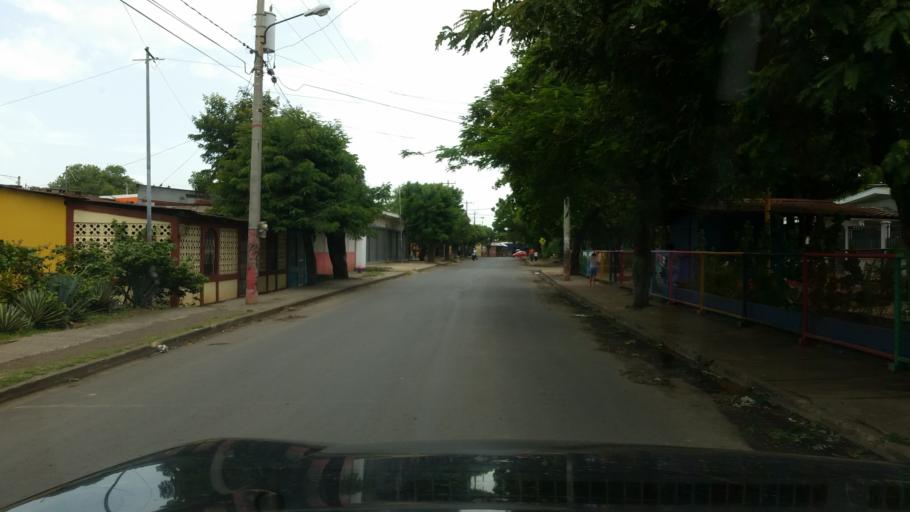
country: NI
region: Managua
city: Managua
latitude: 12.1362
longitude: -86.2186
